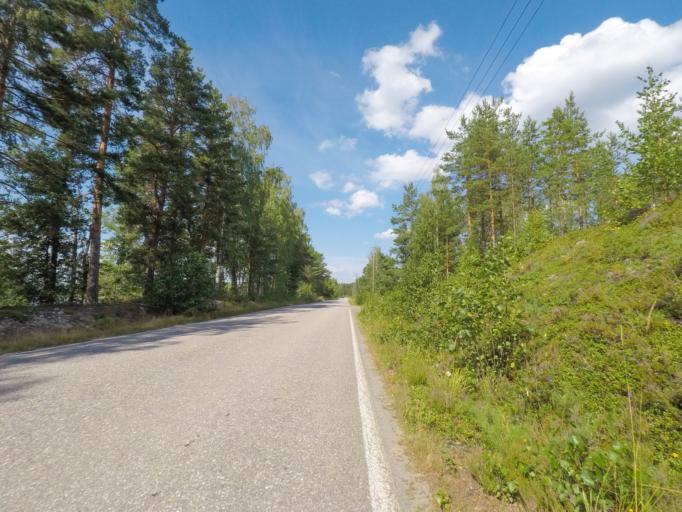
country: FI
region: Southern Savonia
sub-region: Mikkeli
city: Puumala
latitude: 61.4893
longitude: 28.1664
